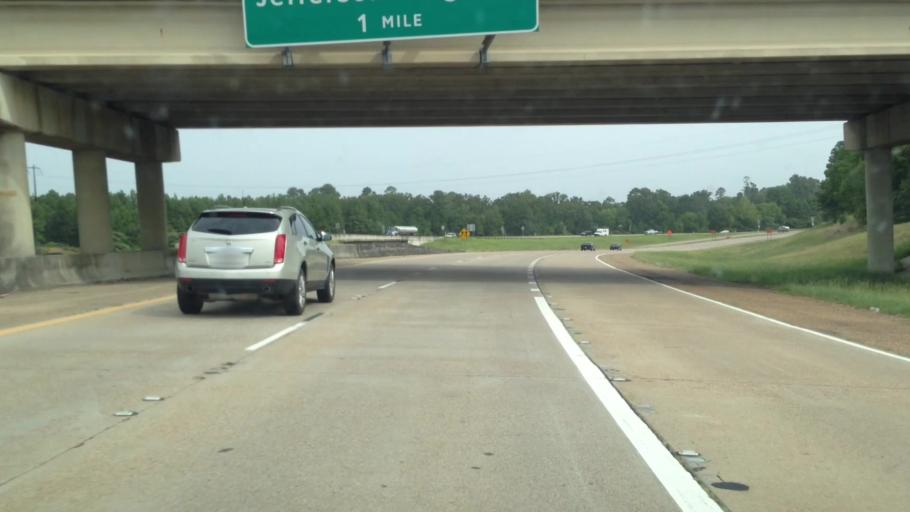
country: US
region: Louisiana
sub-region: Caddo Parish
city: Shreveport
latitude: 32.4583
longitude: -93.8453
